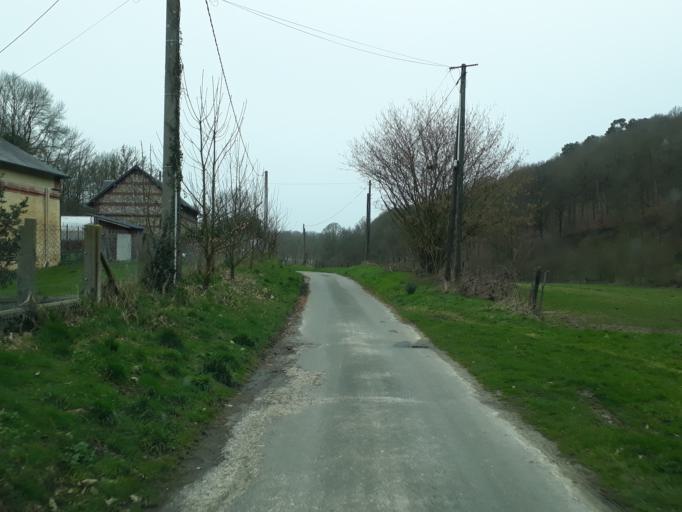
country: FR
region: Haute-Normandie
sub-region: Departement de la Seine-Maritime
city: Les Loges
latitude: 49.6699
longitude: 0.2782
